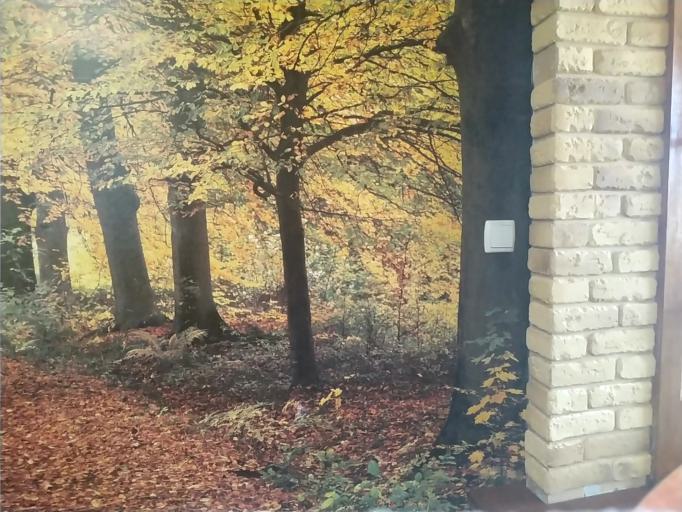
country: RU
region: Tverskaya
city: Krasnomayskiy
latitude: 57.7162
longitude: 34.4777
